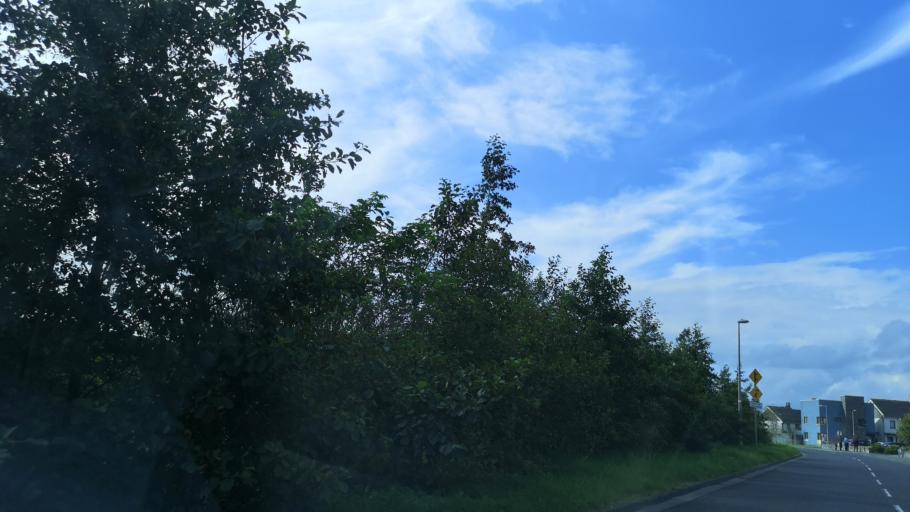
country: IE
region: Connaught
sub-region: County Galway
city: Athenry
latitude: 53.2995
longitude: -8.7541
